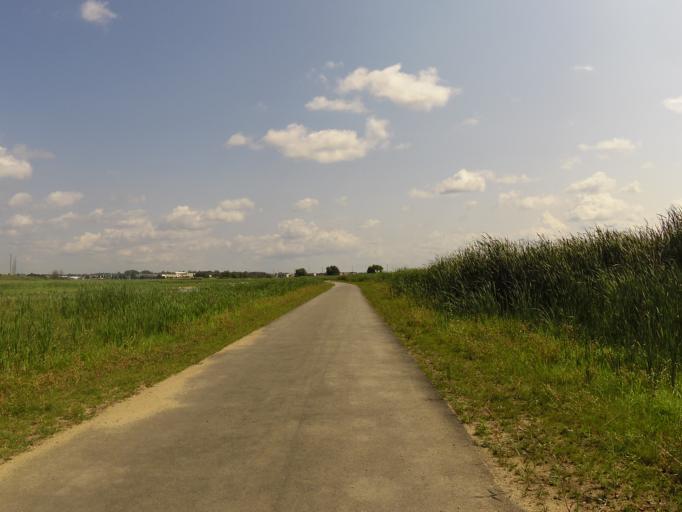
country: CA
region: Ontario
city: Bells Corners
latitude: 45.3094
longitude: -75.9329
